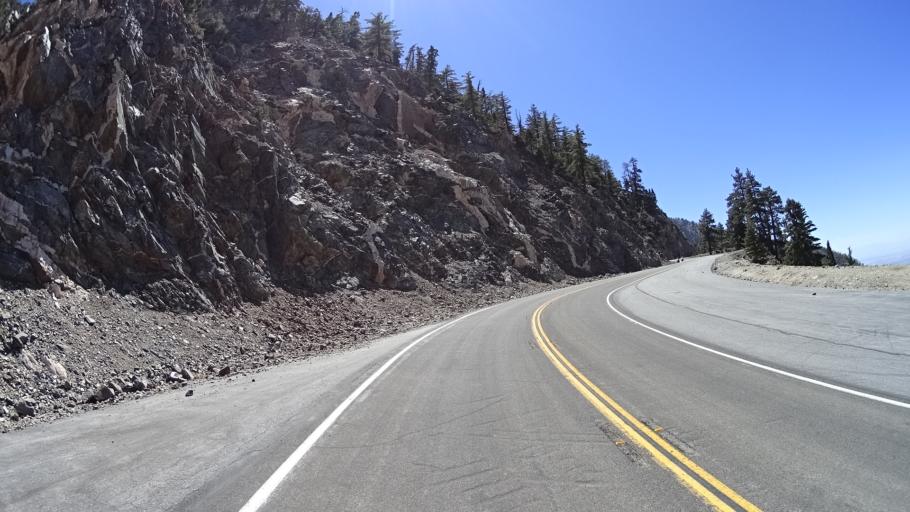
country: US
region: California
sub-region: San Bernardino County
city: Wrightwood
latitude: 34.3672
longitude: -117.7820
